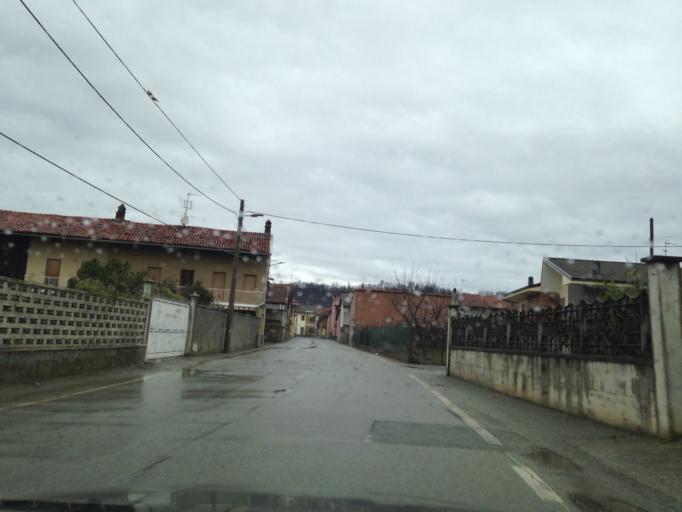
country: IT
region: Piedmont
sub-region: Provincia di Torino
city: Villareggia
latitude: 45.3084
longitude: 7.9773
